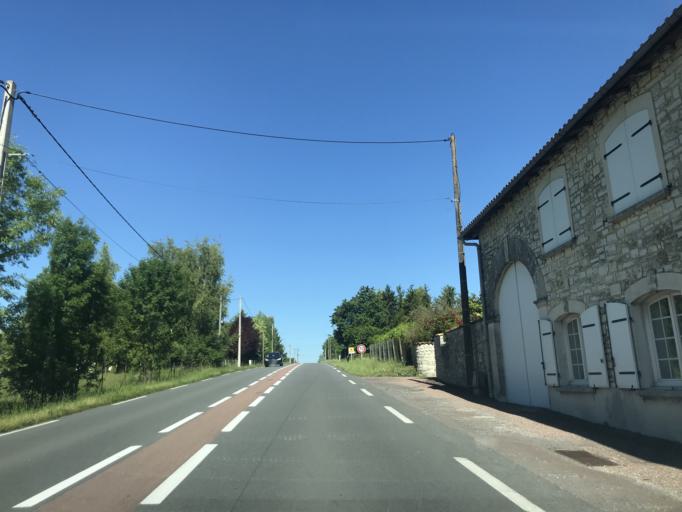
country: FR
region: Poitou-Charentes
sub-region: Departement de la Charente
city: Barbezieux-Saint-Hilaire
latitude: 45.4787
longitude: -0.1662
